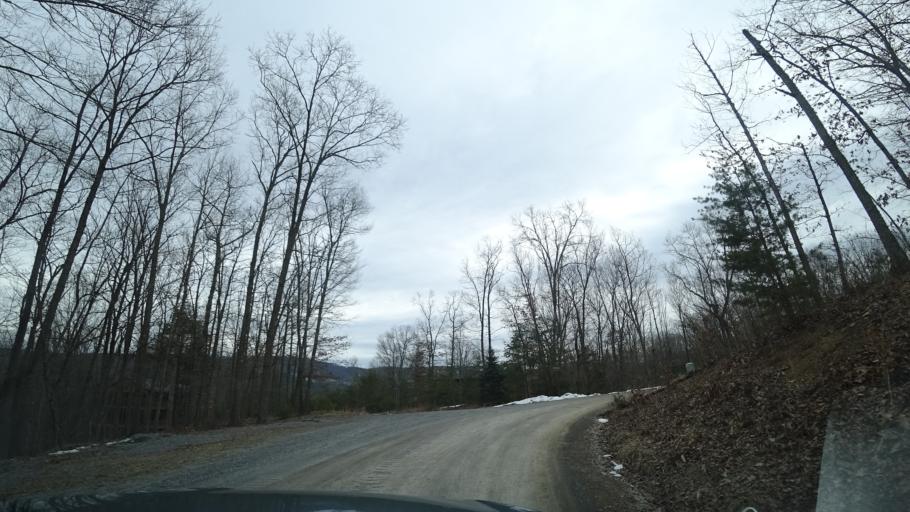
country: US
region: West Virginia
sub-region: Hardy County
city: Moorefield
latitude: 39.0141
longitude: -78.7741
